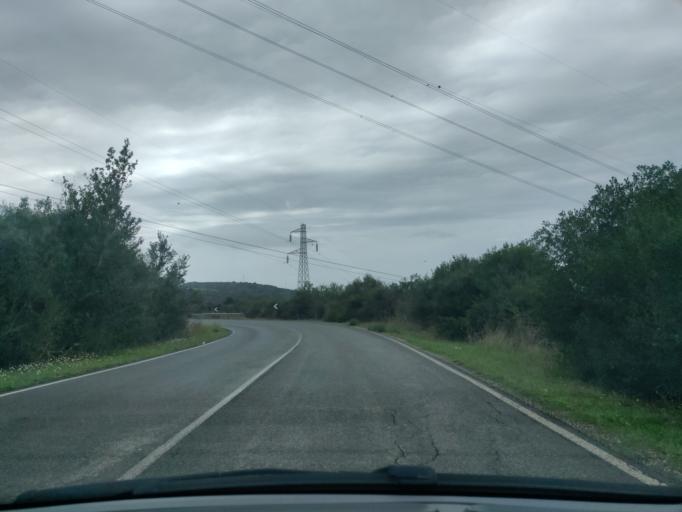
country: IT
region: Latium
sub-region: Citta metropolitana di Roma Capitale
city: Allumiere
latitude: 42.1238
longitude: 11.8635
